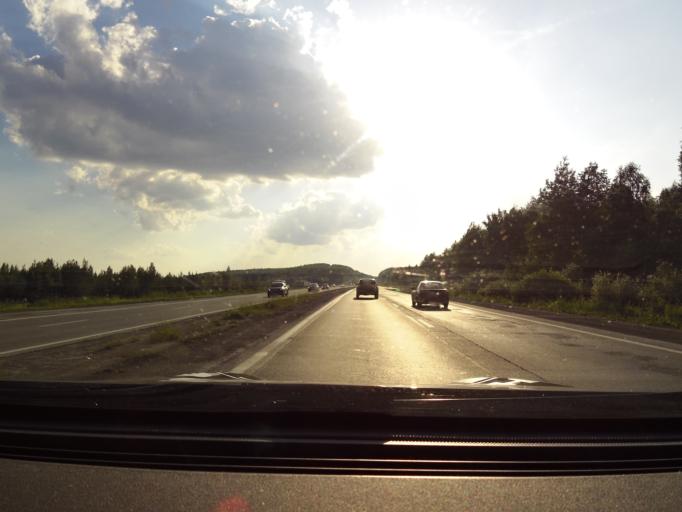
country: RU
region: Sverdlovsk
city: Talitsa
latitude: 56.8377
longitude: 60.1463
